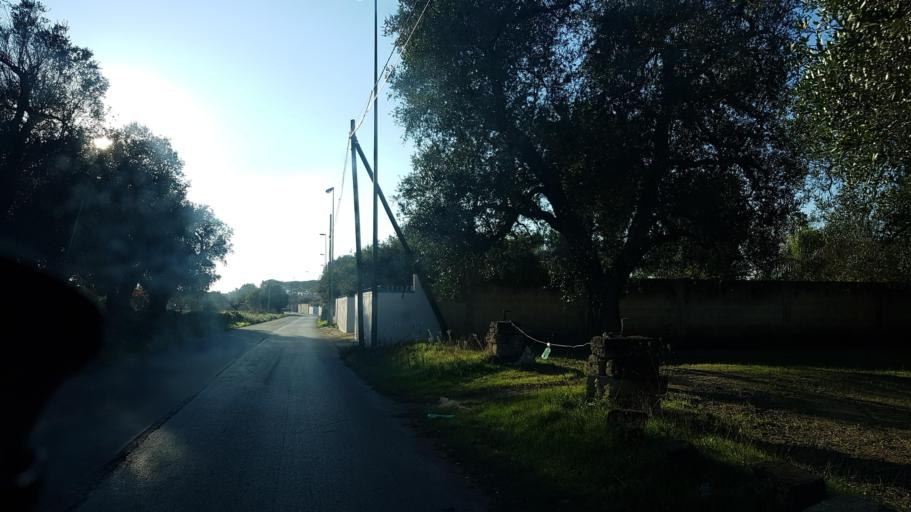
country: IT
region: Apulia
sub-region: Provincia di Brindisi
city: Latiano
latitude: 40.5581
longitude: 17.7323
